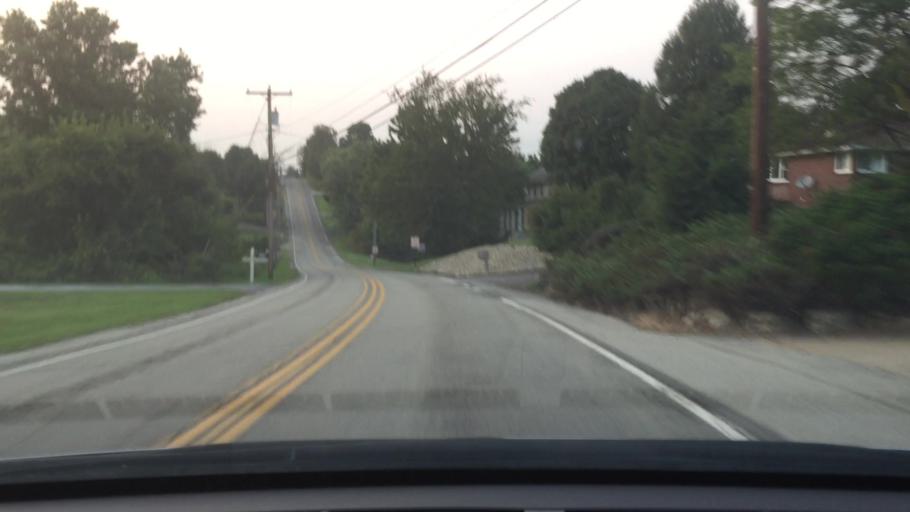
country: US
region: Pennsylvania
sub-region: Westmoreland County
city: Fellsburg
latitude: 40.1761
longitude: -79.8210
